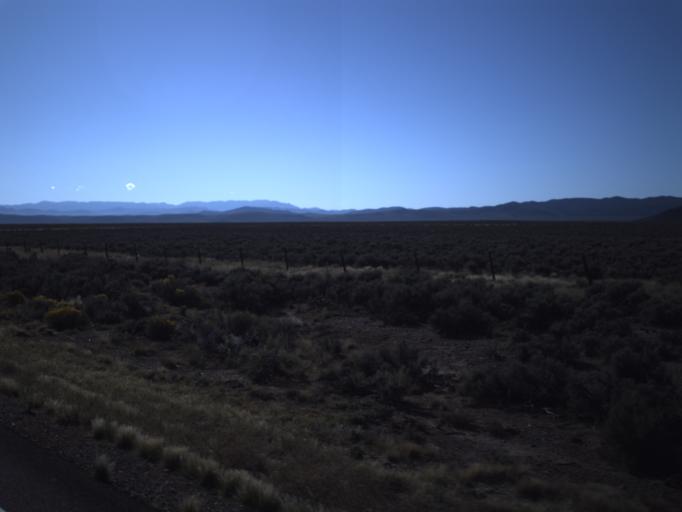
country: US
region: Utah
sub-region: Washington County
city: Enterprise
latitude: 37.7950
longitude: -113.9008
